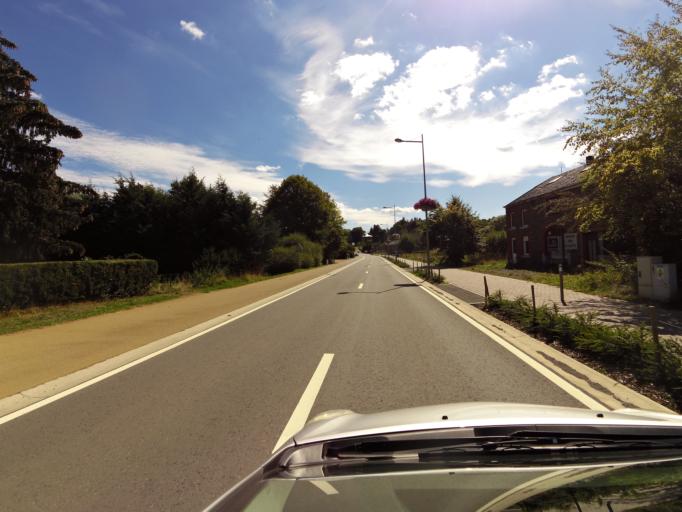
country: BE
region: Wallonia
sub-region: Province du Luxembourg
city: Rendeux
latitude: 50.2328
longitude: 5.5127
